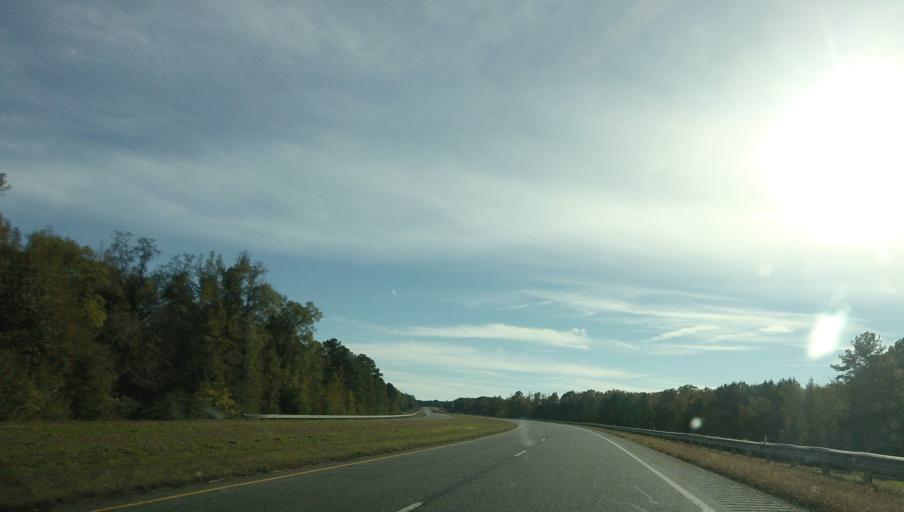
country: US
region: Georgia
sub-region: Taylor County
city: Butler
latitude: 32.7275
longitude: -84.2315
